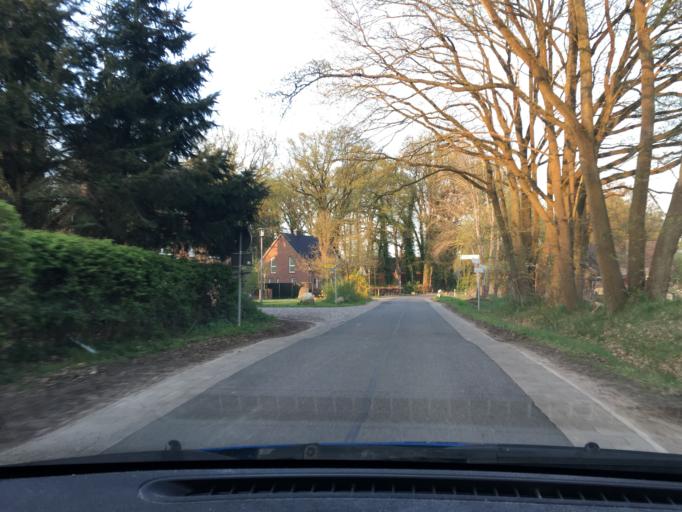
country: DE
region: Lower Saxony
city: Sudergellersen
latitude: 53.2071
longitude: 10.2919
